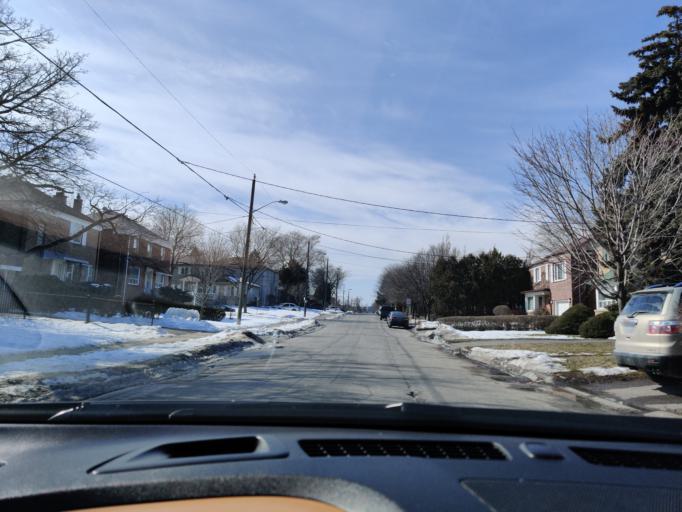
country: CA
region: Ontario
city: Toronto
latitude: 43.7174
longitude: -79.4343
